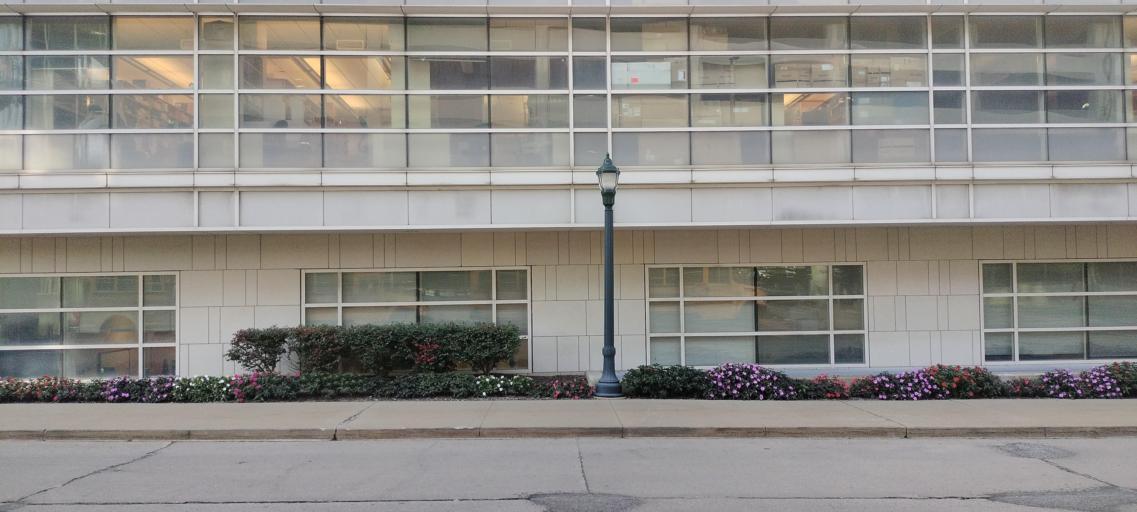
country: US
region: Ohio
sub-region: Cuyahoga County
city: East Cleveland
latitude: 41.5062
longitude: -81.6027
